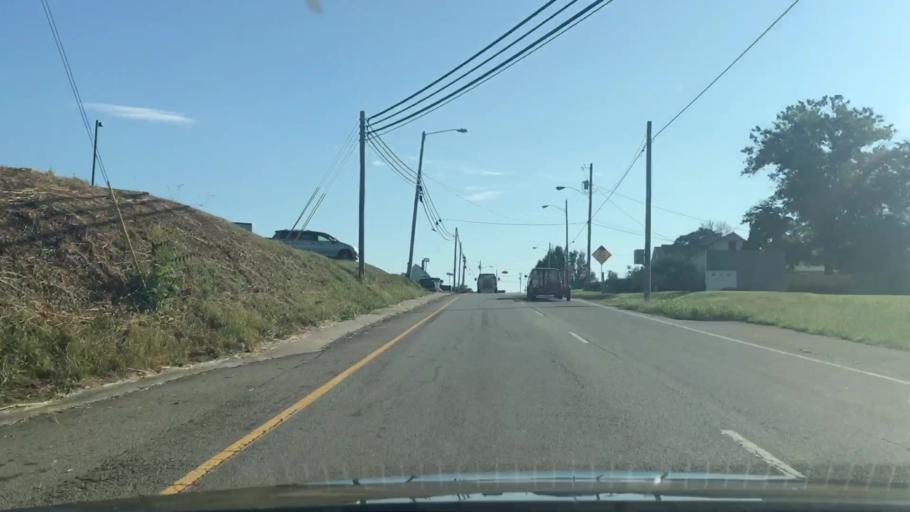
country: US
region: Tennessee
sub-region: Overton County
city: Livingston
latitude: 36.3811
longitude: -85.3284
